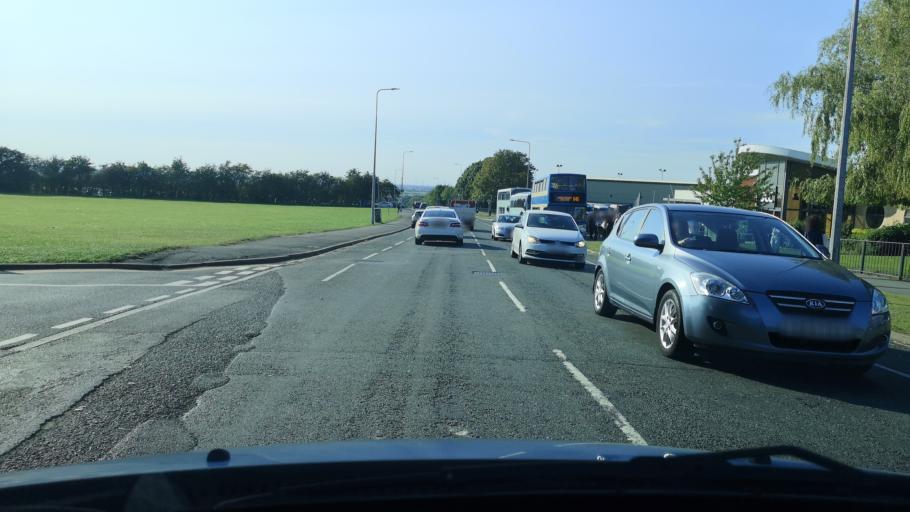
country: GB
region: England
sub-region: North Lincolnshire
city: Scunthorpe
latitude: 53.5739
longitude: -0.6665
